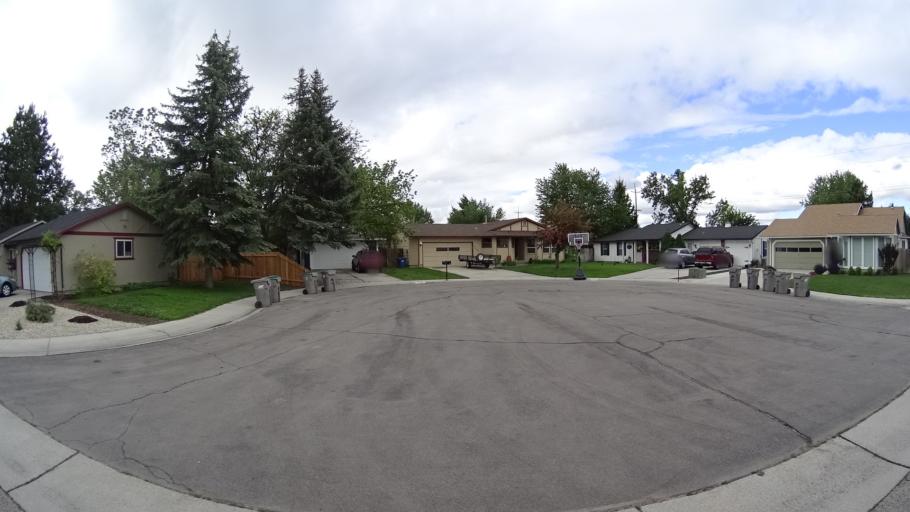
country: US
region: Idaho
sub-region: Ada County
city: Garden City
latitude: 43.6779
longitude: -116.2784
